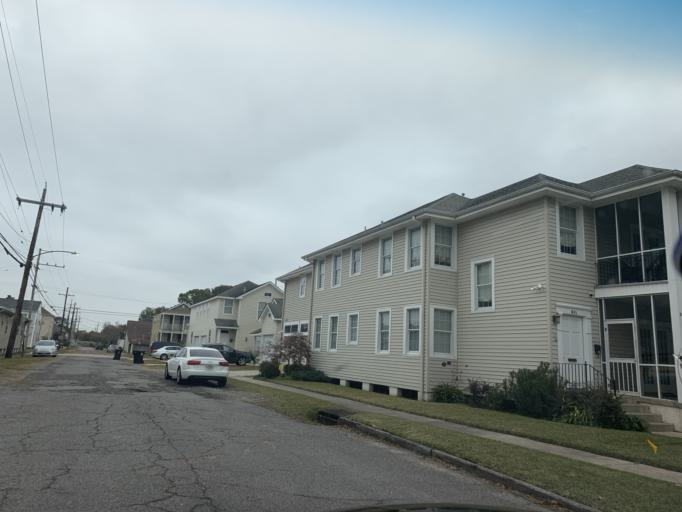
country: US
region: Louisiana
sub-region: Jefferson Parish
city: Metairie
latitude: 29.9897
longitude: -90.1068
